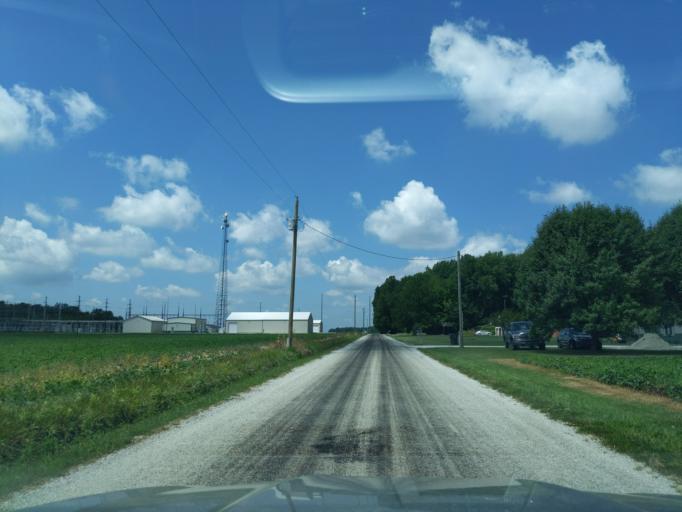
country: US
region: Indiana
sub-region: Ripley County
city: Osgood
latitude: 39.2191
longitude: -85.3418
